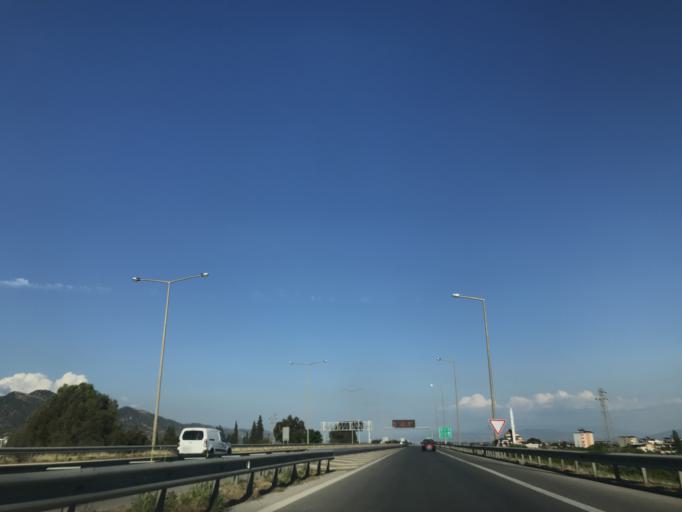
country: TR
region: Aydin
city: Germencik
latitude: 37.8818
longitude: 27.5870
